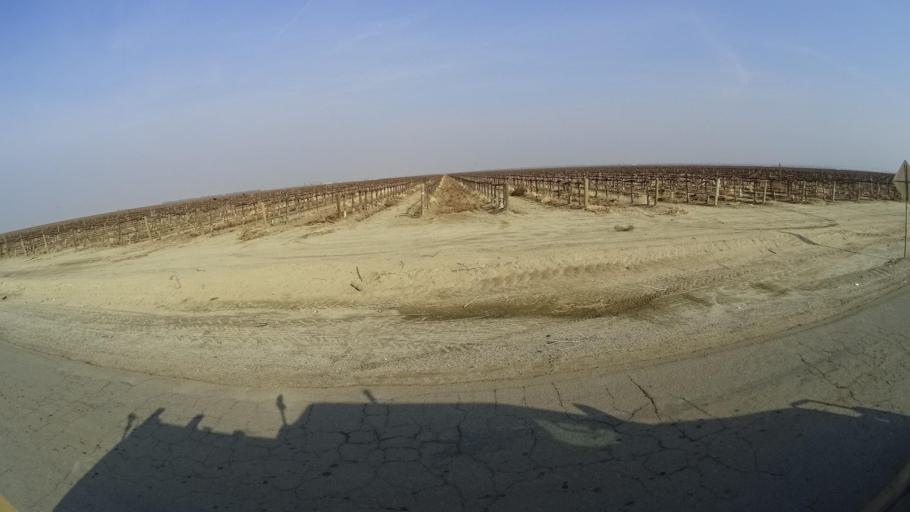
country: US
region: California
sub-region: Kern County
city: Lebec
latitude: 34.9930
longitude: -118.9033
